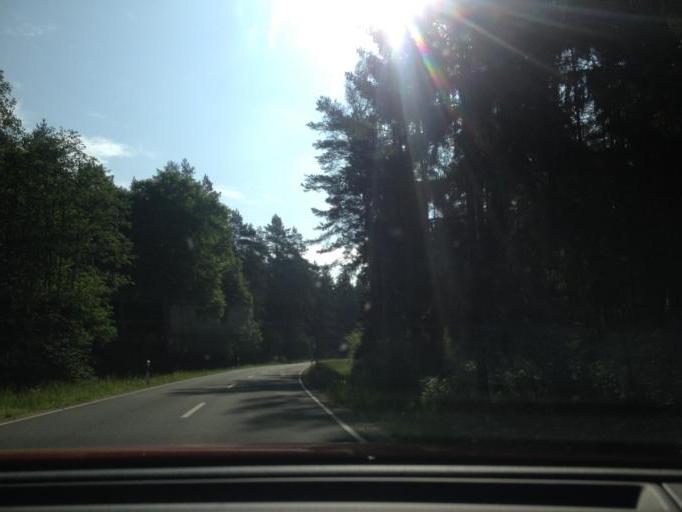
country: DE
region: Bavaria
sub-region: Upper Palatinate
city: Speinshart
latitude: 49.7782
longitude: 11.7795
